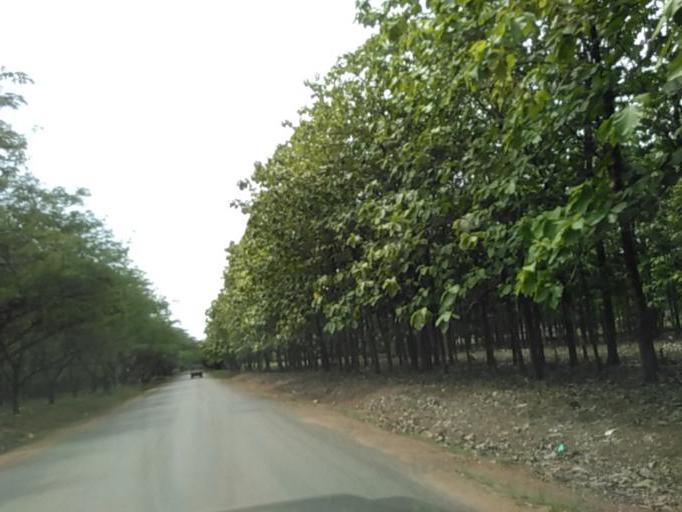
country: GH
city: Akropong
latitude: 6.0946
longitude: 0.1058
